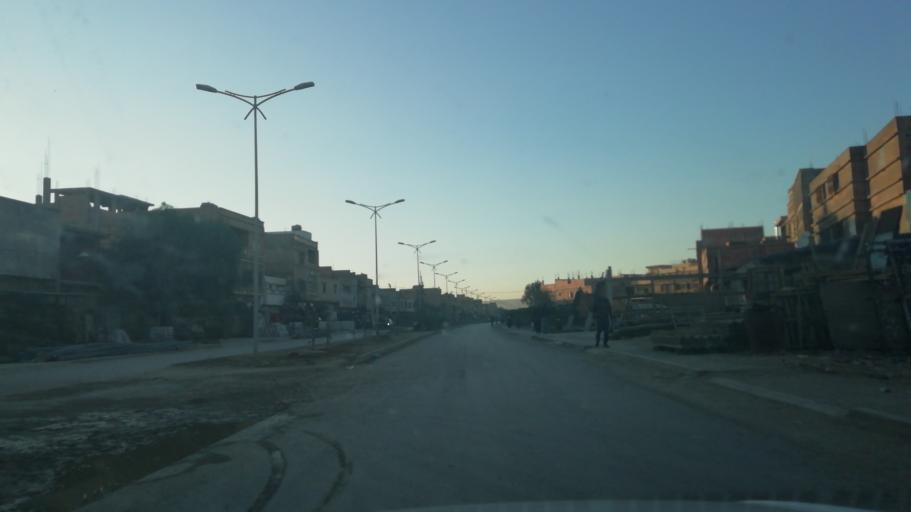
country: DZ
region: Oran
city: Es Senia
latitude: 35.6484
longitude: -0.5731
